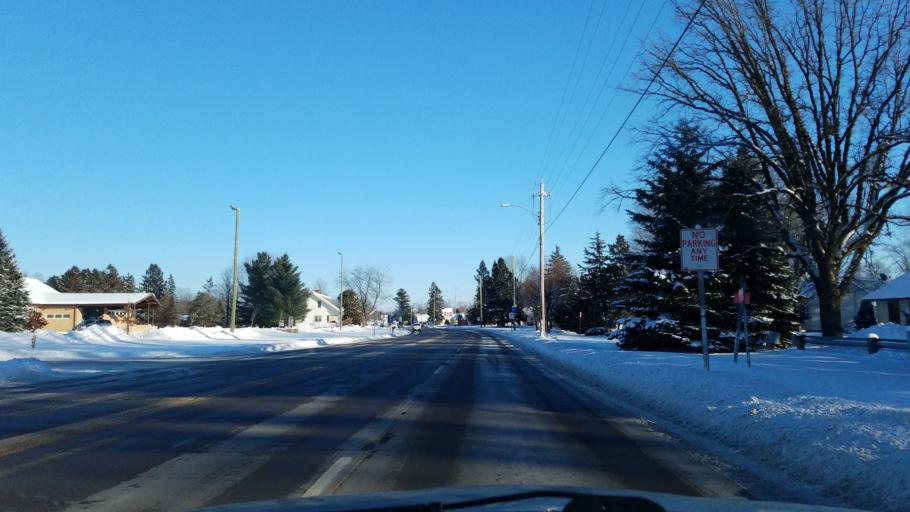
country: US
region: Wisconsin
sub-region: Barron County
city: Rice Lake
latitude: 45.5089
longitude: -91.7477
